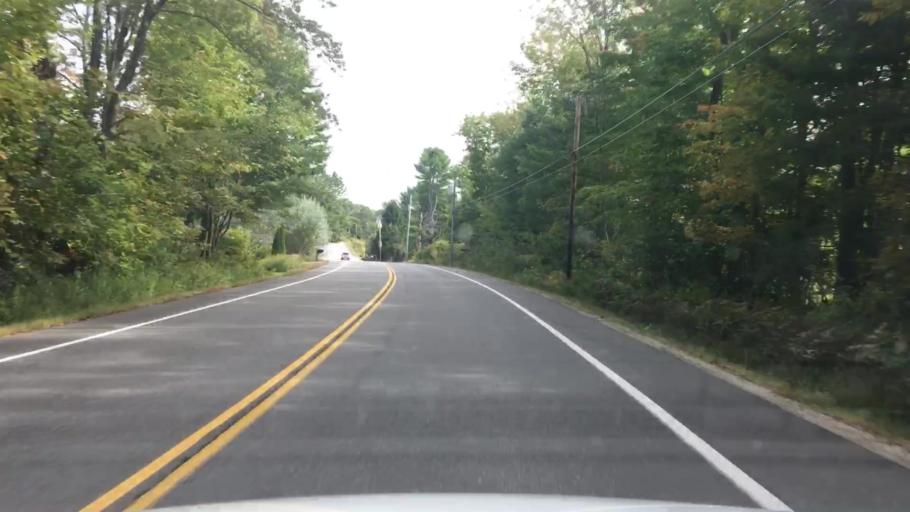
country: US
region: Maine
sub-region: Androscoggin County
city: Lisbon Falls
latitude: 43.9544
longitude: -70.0419
